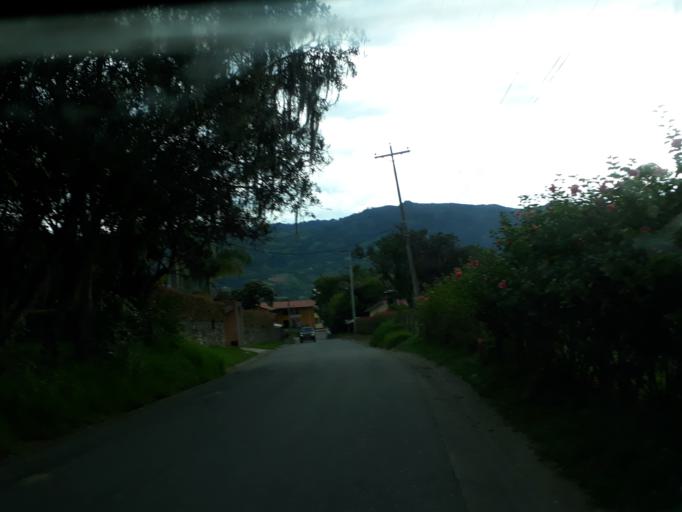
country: CO
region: Cundinamarca
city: Pacho
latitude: 5.1556
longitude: -74.1404
